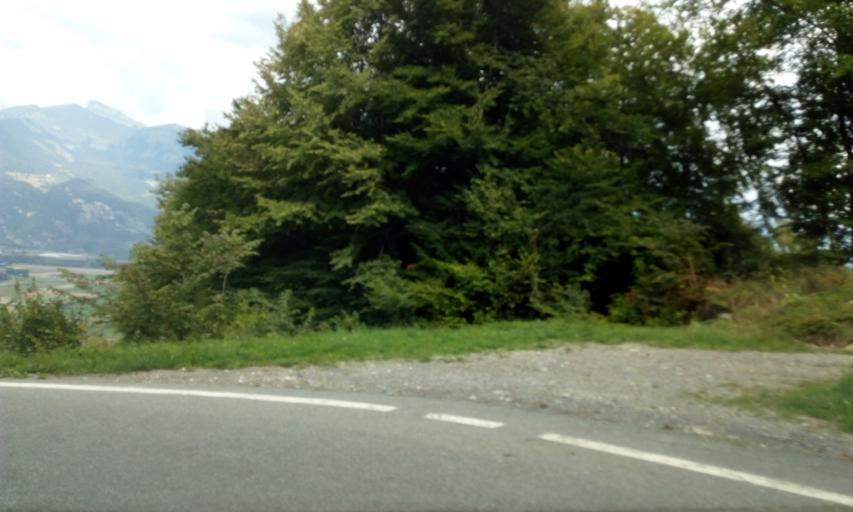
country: CH
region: Valais
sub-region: Monthey District
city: Vionnaz
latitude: 46.3068
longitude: 6.8919
